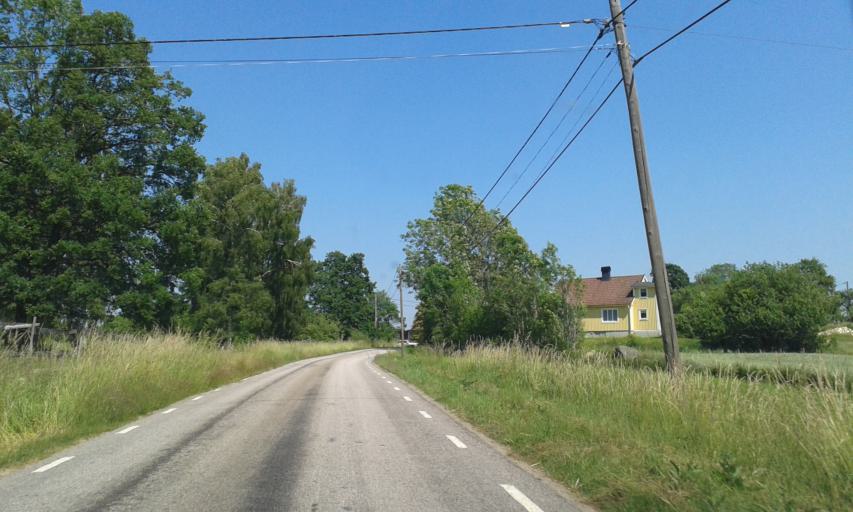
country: SE
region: Blekinge
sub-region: Karlskrona Kommun
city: Rodeby
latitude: 56.2572
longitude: 15.5465
